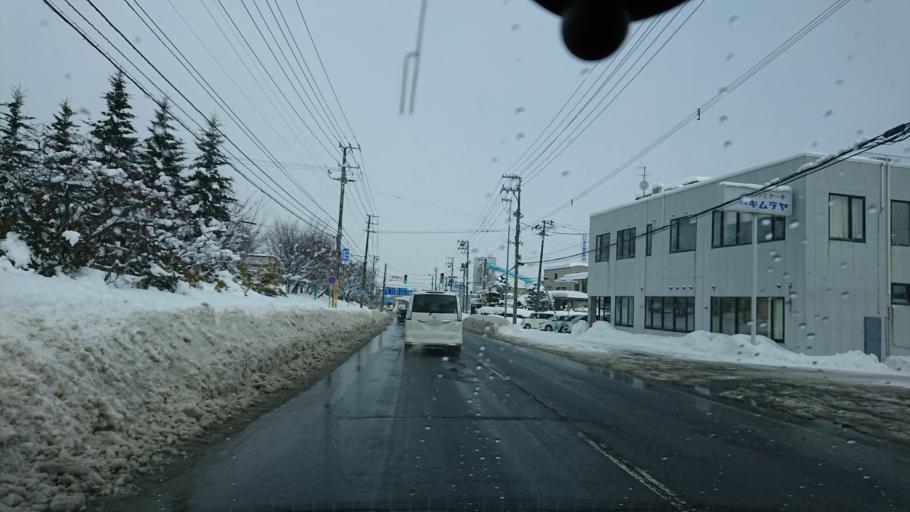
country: JP
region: Hokkaido
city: Sapporo
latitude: 42.9703
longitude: 141.3435
